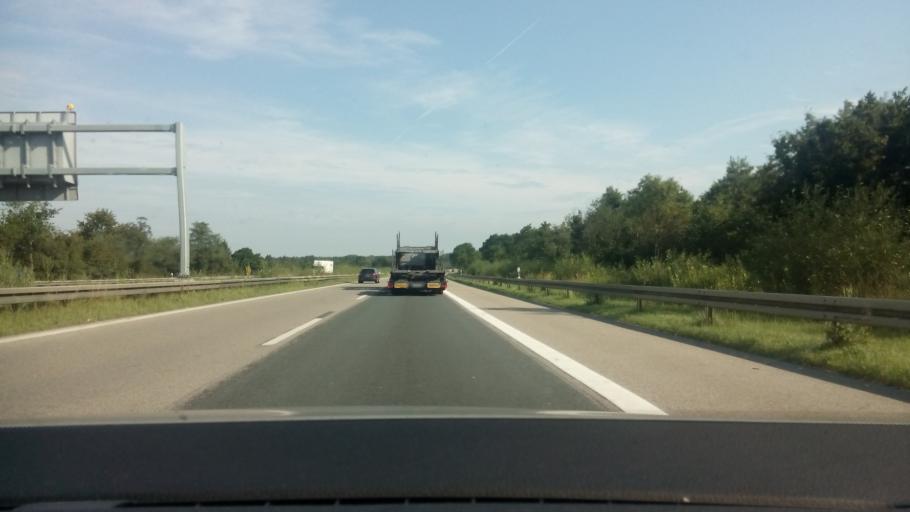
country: DE
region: Bavaria
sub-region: Upper Bavaria
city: Oberschleissheim
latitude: 48.2392
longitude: 11.5369
